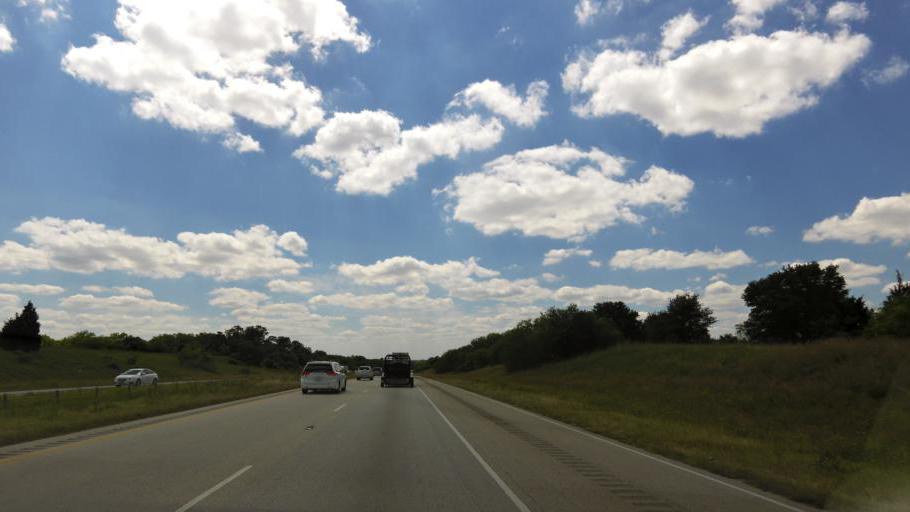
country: US
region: Texas
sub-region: Colorado County
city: Weimar
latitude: 29.6884
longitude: -96.8249
